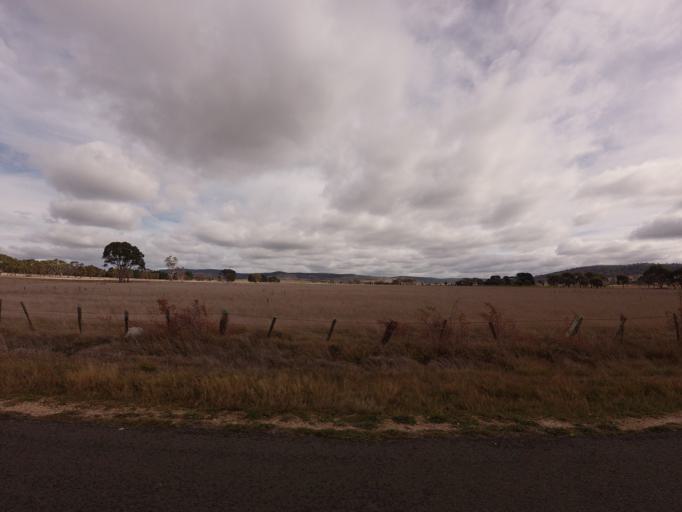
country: AU
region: Tasmania
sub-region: Brighton
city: Bridgewater
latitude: -42.4069
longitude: 147.3956
